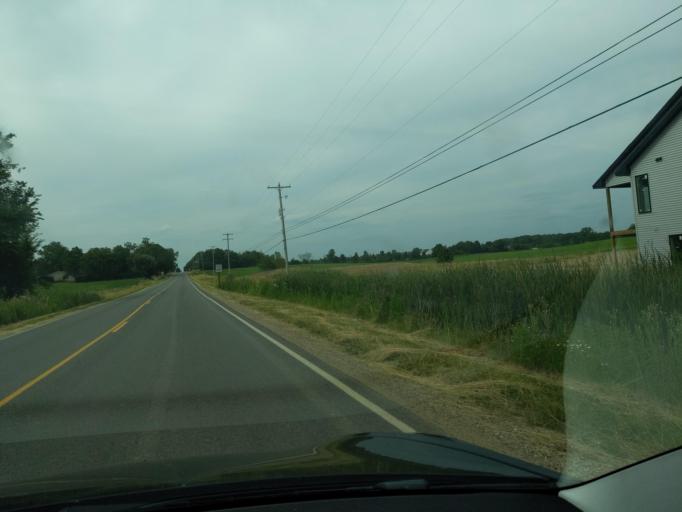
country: US
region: Michigan
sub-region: Clinton County
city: DeWitt
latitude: 42.8426
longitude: -84.6025
